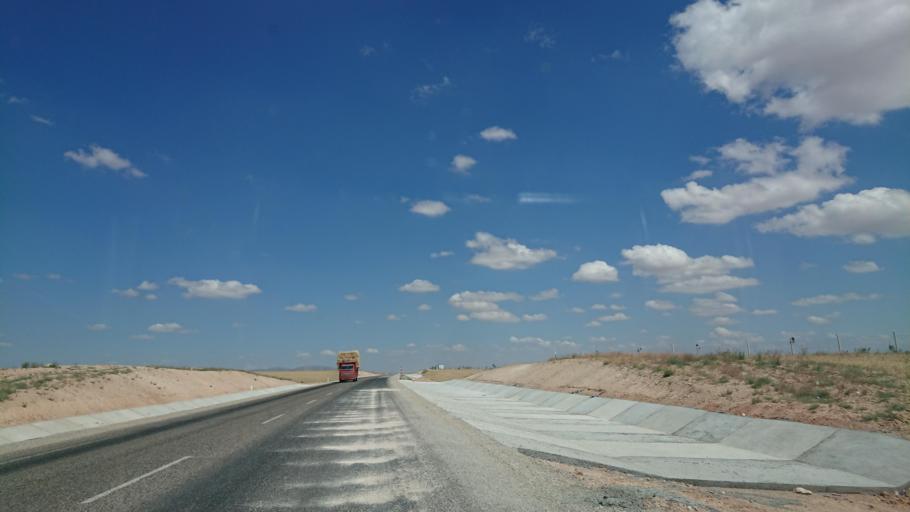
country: TR
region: Kirsehir
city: Kirsehir
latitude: 39.1239
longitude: 33.9924
